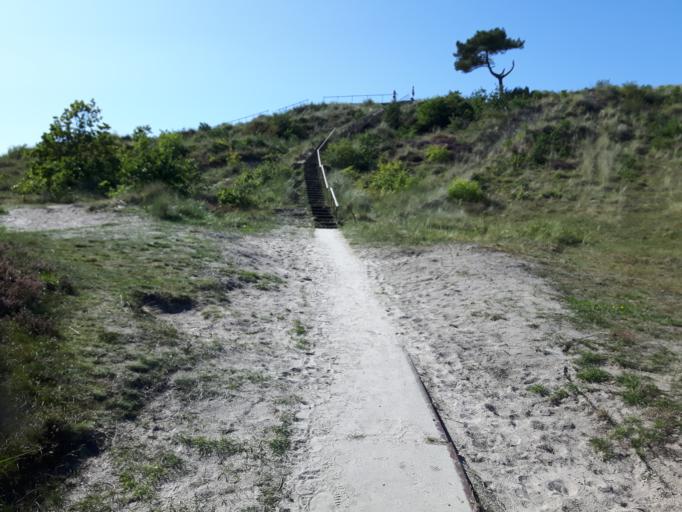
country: NL
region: Friesland
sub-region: Gemeente Terschelling
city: West-Terschelling
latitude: 53.3828
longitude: 5.2545
